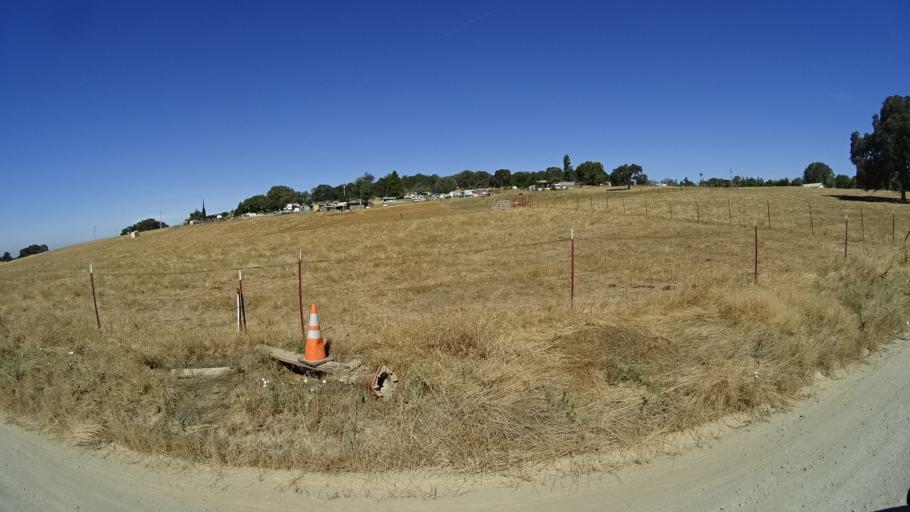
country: US
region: California
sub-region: Amador County
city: Jackson
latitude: 38.2682
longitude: -120.7643
